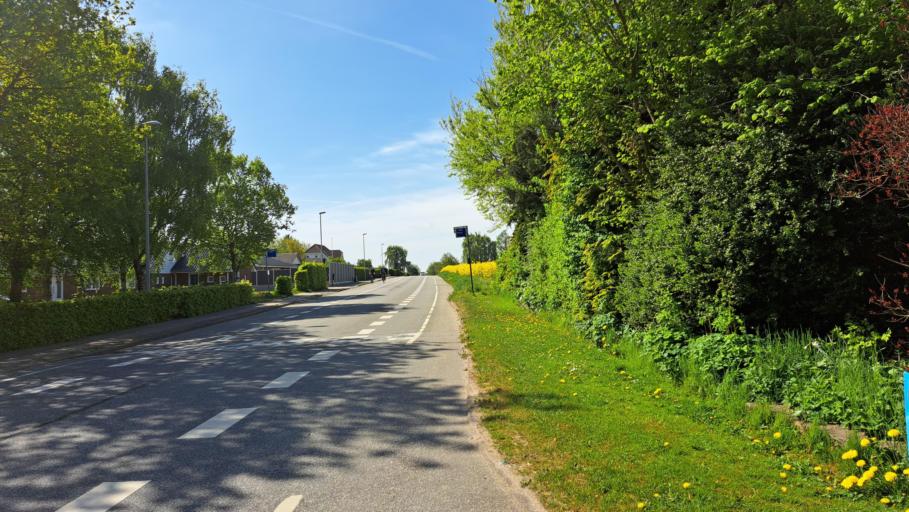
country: DK
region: Central Jutland
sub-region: Hedensted Kommune
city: Hedensted
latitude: 55.8033
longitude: 9.6471
